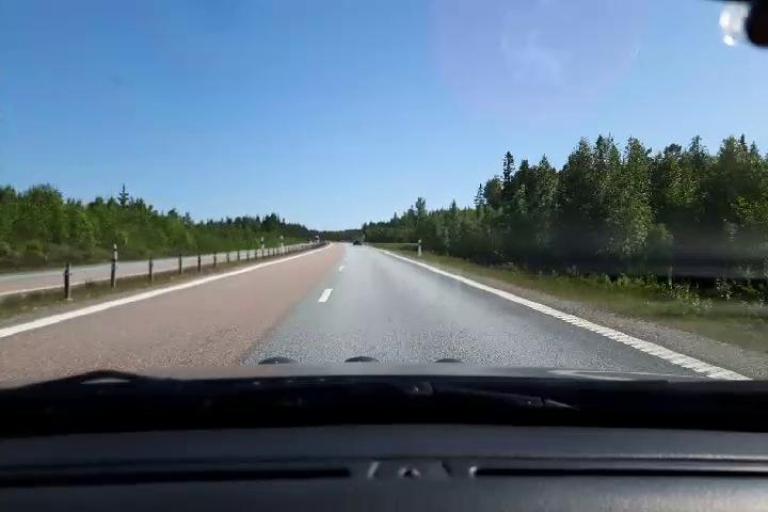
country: SE
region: Gaevleborg
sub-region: Soderhamns Kommun
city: Soderhamn
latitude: 61.4155
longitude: 16.9887
